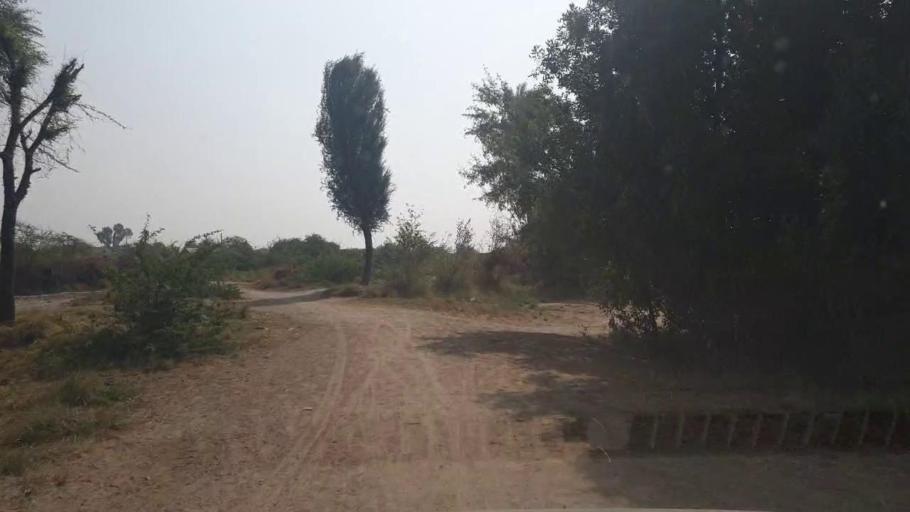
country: PK
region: Sindh
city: Umarkot
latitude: 25.4276
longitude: 69.6541
